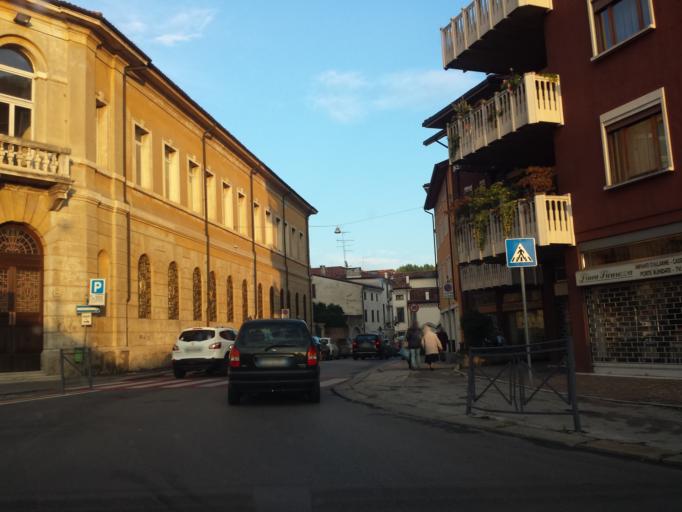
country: IT
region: Veneto
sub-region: Provincia di Vicenza
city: Vicenza
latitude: 45.5543
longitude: 11.5415
